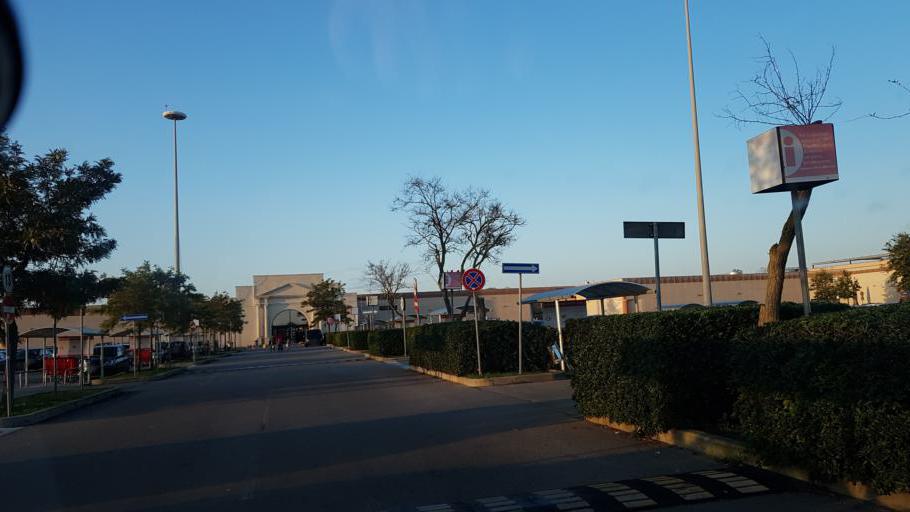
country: IT
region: Apulia
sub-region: Provincia di Lecce
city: Giorgilorio
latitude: 40.3751
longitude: 18.1437
